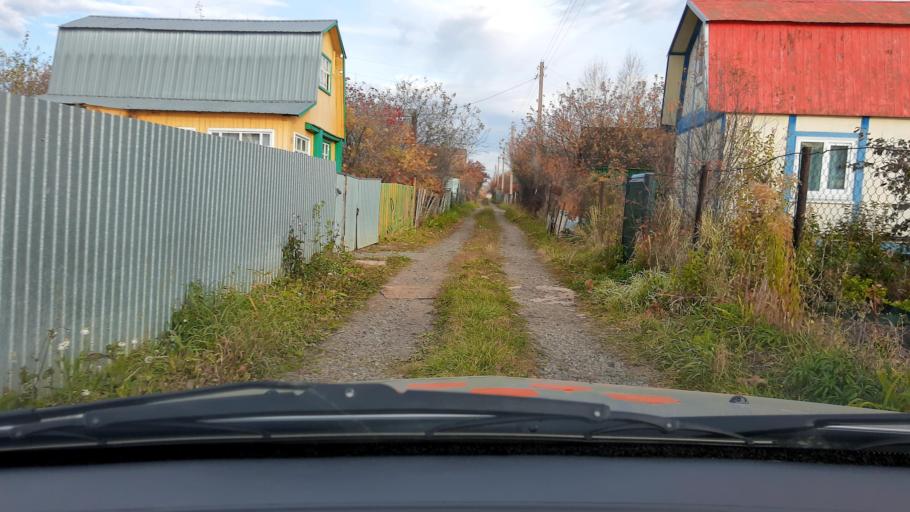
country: RU
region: Bashkortostan
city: Asanovo
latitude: 54.8042
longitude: 55.6127
